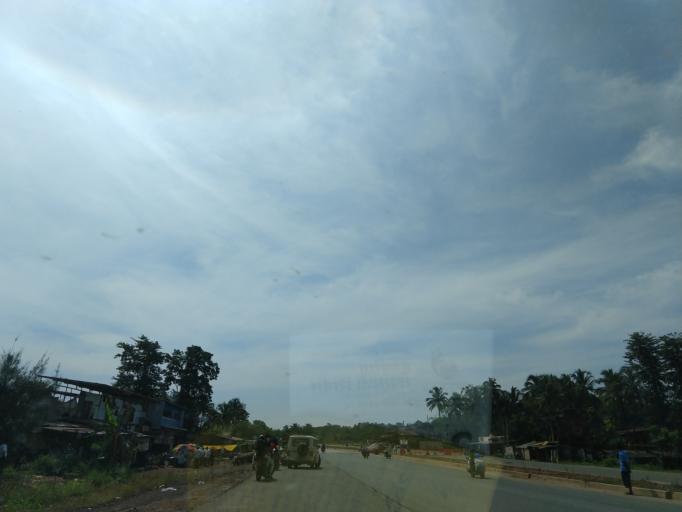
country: IN
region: Maharashtra
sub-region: Sindhudurg
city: Kudal
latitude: 15.9518
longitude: 73.7391
